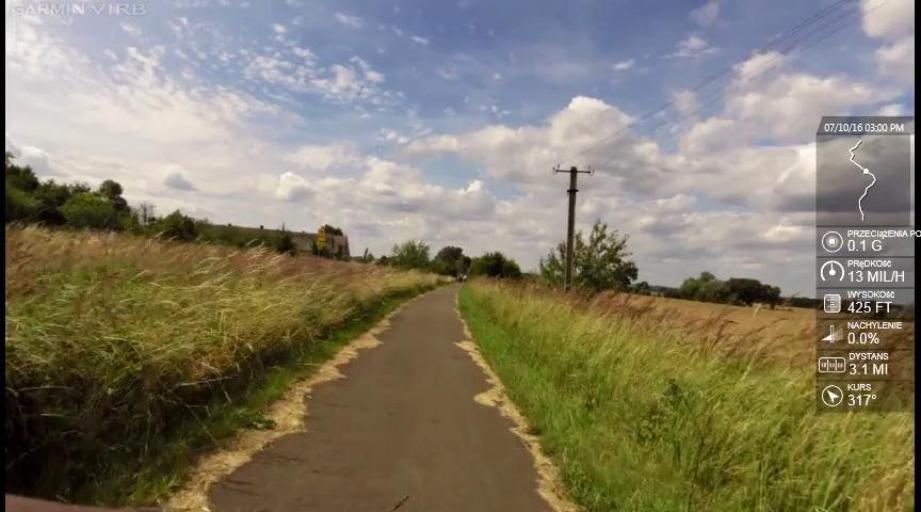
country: PL
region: West Pomeranian Voivodeship
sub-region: Powiat gryfinski
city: Banie
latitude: 53.1091
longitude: 14.6366
